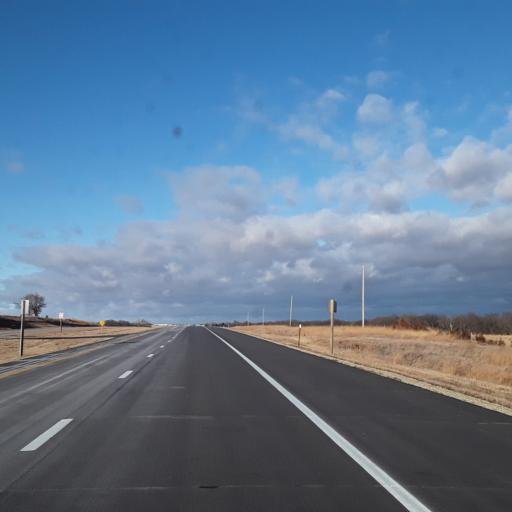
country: US
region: Kansas
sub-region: Republic County
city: Belleville
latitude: 39.9504
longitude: -97.6135
